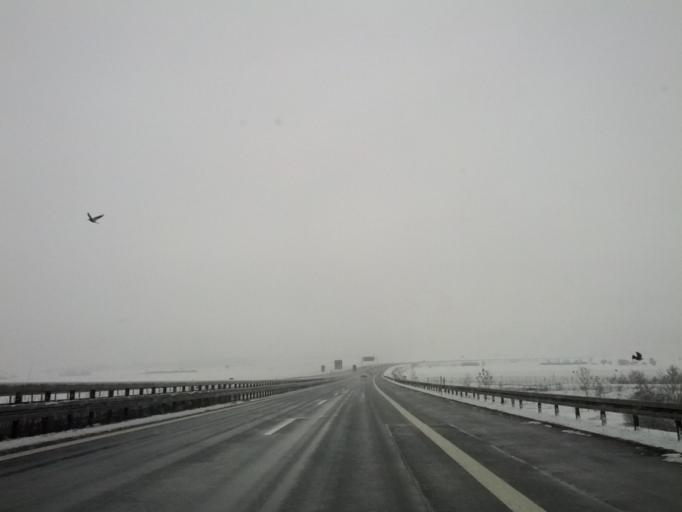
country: DE
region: Bavaria
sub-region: Regierungsbezirk Unterfranken
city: Geldersheim
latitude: 50.0249
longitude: 10.1509
